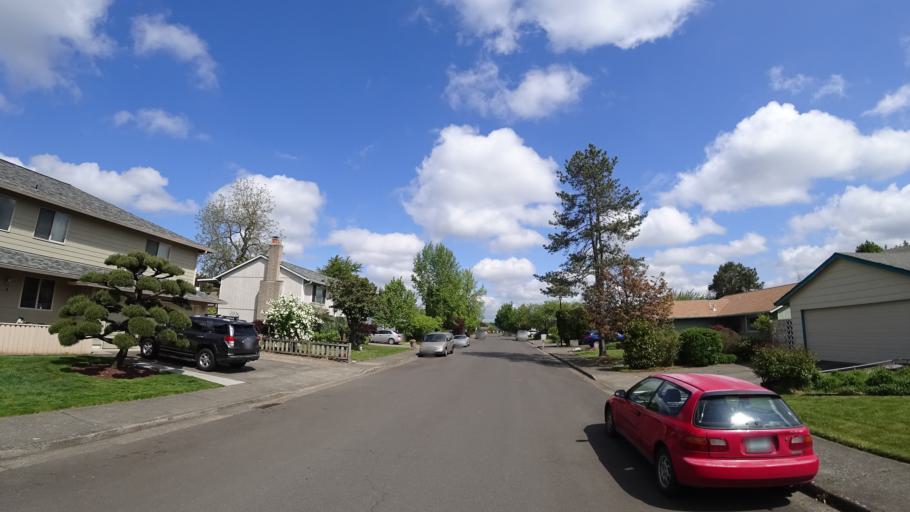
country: US
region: Oregon
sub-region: Washington County
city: Aloha
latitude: 45.5081
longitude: -122.8909
